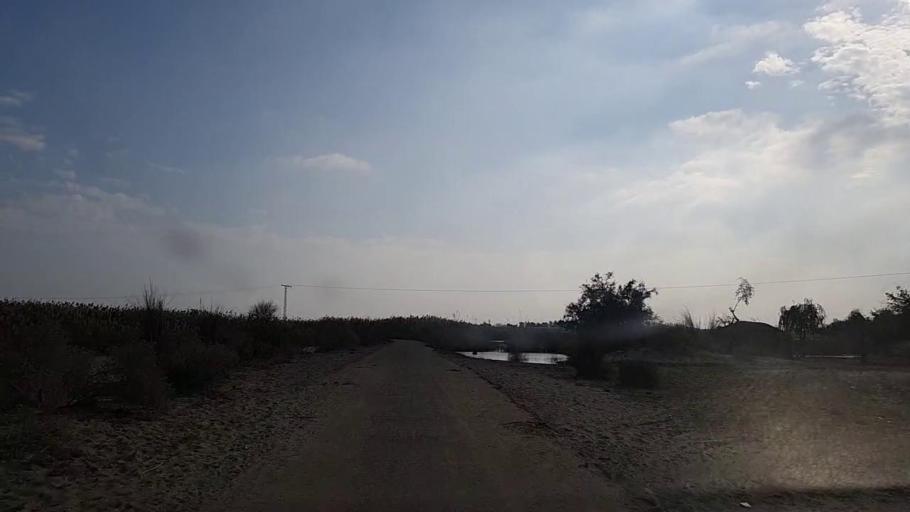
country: PK
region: Sindh
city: Sanghar
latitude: 26.2061
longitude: 69.0214
